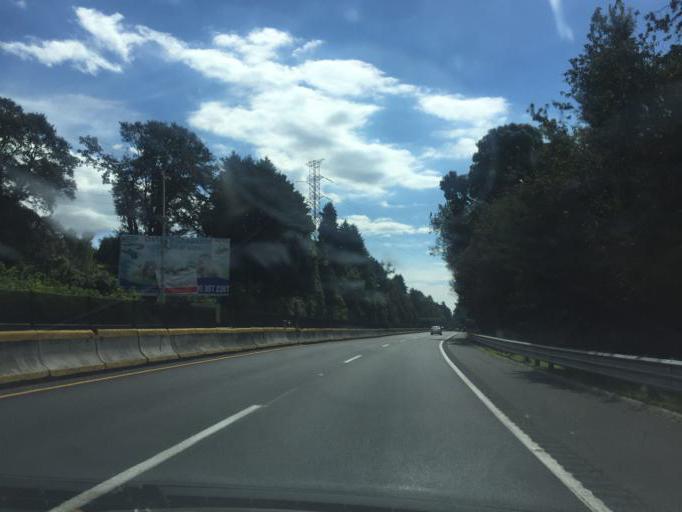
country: MX
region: Morelos
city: Tres Marias
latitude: 19.0470
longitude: -99.2371
